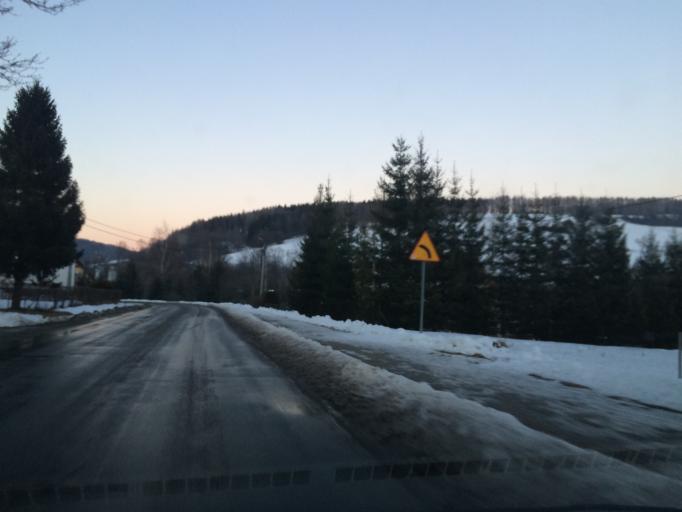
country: PL
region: Subcarpathian Voivodeship
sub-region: Powiat bieszczadzki
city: Ustrzyki Dolne
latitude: 49.4201
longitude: 22.5755
